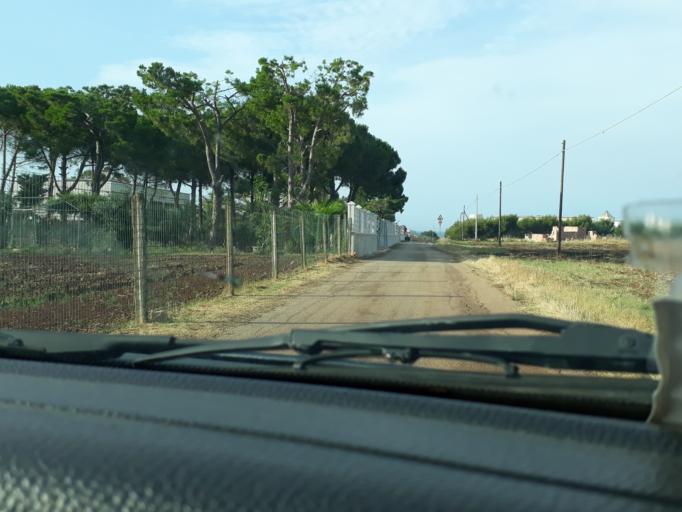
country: IT
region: Apulia
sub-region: Provincia di Brindisi
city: Carovigno
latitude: 40.7602
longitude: 17.6838
